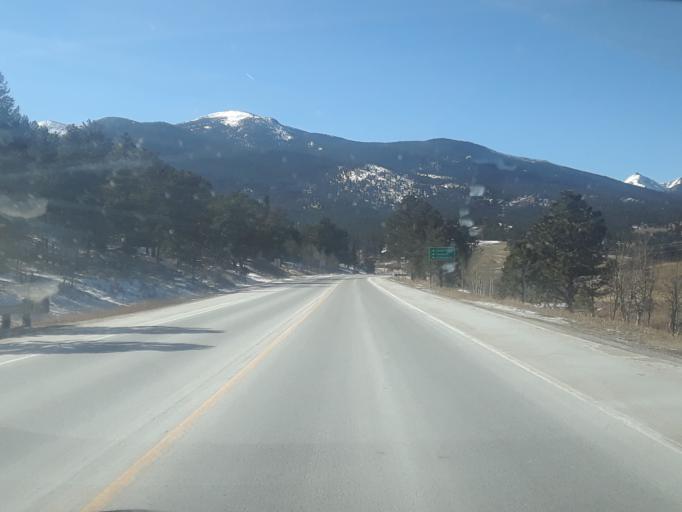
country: US
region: Colorado
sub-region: Larimer County
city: Estes Park
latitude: 40.1885
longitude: -105.5027
